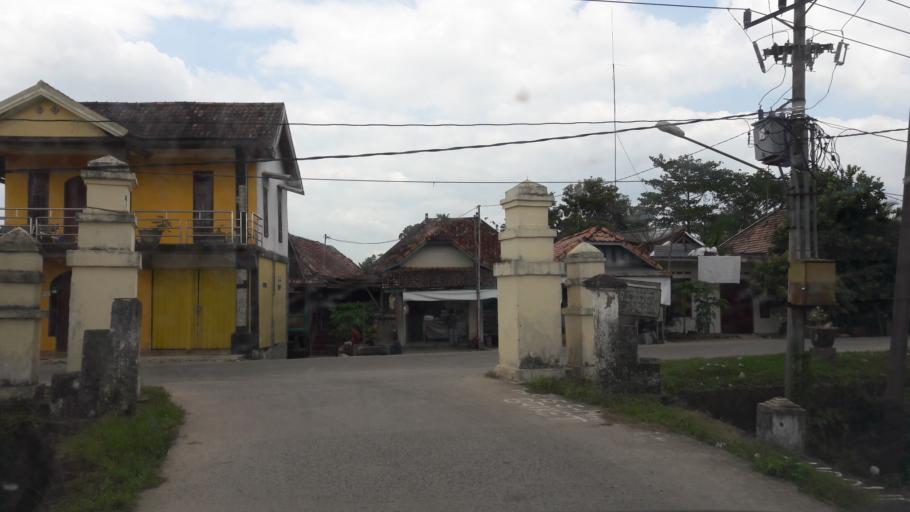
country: ID
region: South Sumatra
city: Prabumulih
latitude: -3.3493
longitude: 104.0921
